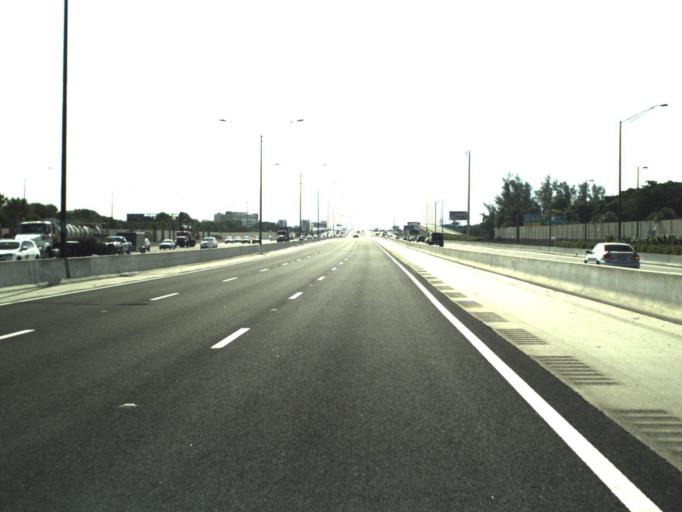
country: US
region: Florida
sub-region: Broward County
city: Pine Island Ridge
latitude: 26.1057
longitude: -80.2772
